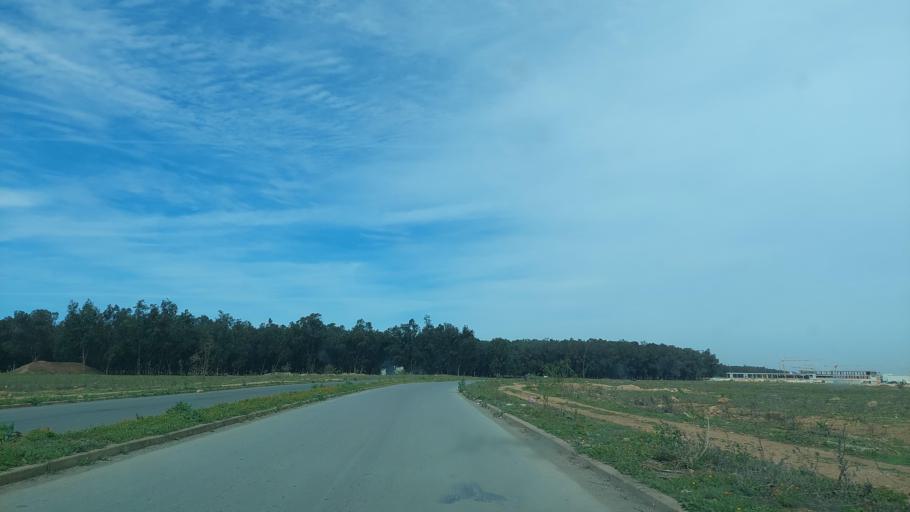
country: MA
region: Grand Casablanca
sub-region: Mediouna
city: Mediouna
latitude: 33.3926
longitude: -7.5483
